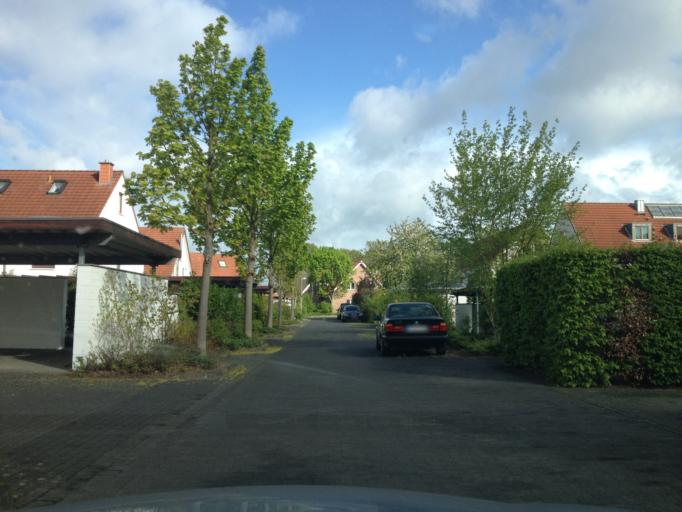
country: DE
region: North Rhine-Westphalia
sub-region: Regierungsbezirk Detmold
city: Guetersloh
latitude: 51.8844
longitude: 8.3999
